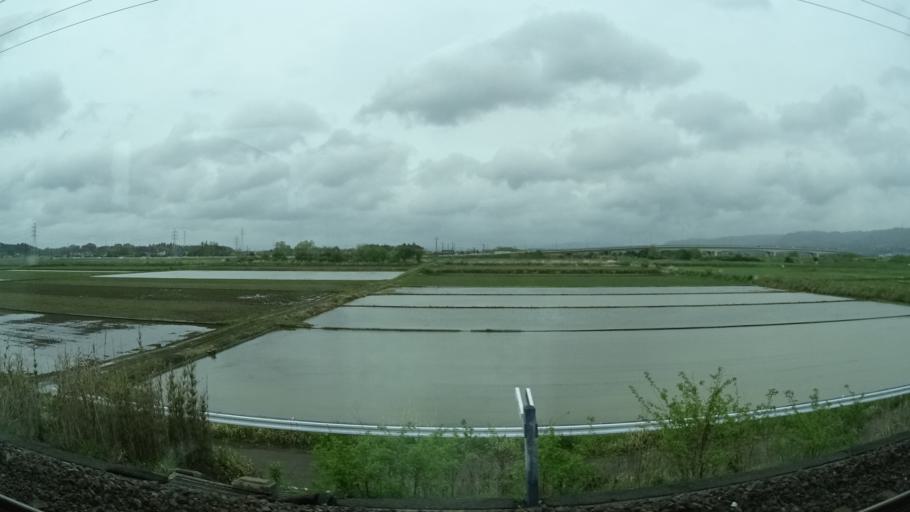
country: JP
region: Ibaraki
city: Funaishikawa
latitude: 36.4834
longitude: 140.5922
